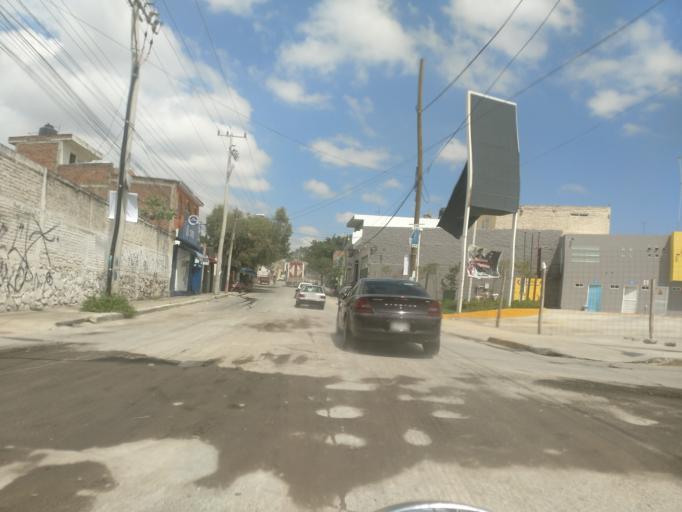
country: MX
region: Jalisco
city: Tlaquepaque
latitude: 20.6460
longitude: -103.2730
